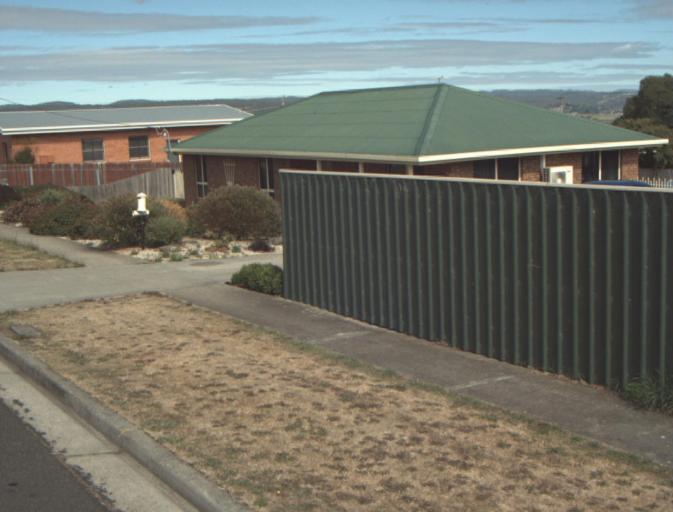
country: AU
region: Tasmania
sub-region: Launceston
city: Mayfield
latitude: -41.3834
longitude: 147.1255
